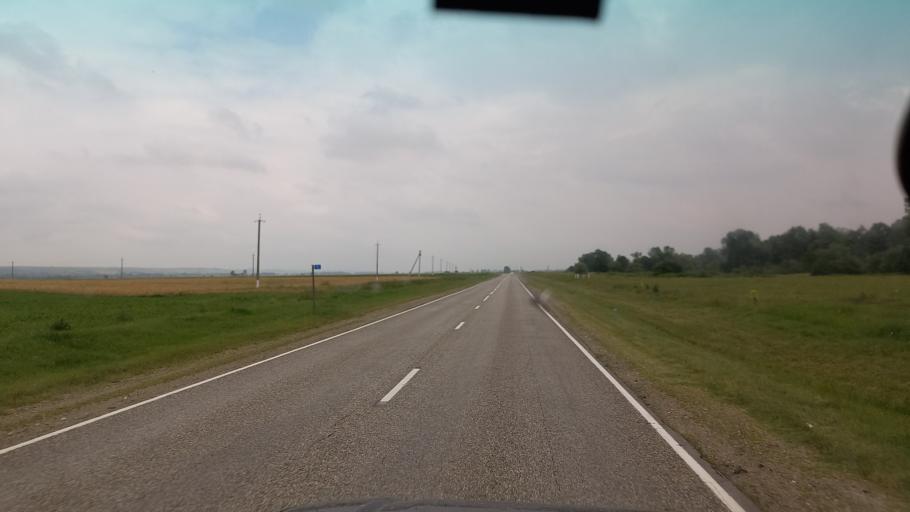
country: RU
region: Adygeya
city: Khodz'
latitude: 44.4759
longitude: 40.7582
